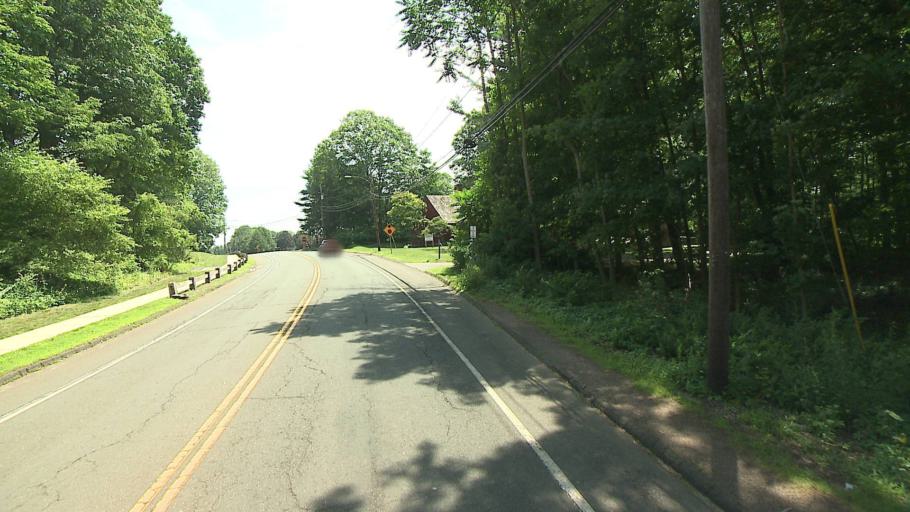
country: US
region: Connecticut
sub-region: New Haven County
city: Hamden
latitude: 41.4203
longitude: -72.9015
